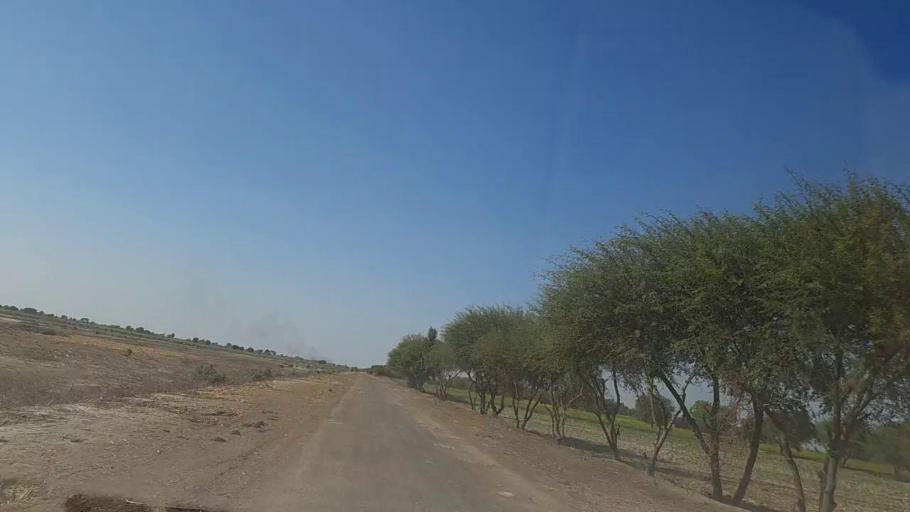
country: PK
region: Sindh
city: Digri
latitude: 25.1172
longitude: 69.0461
